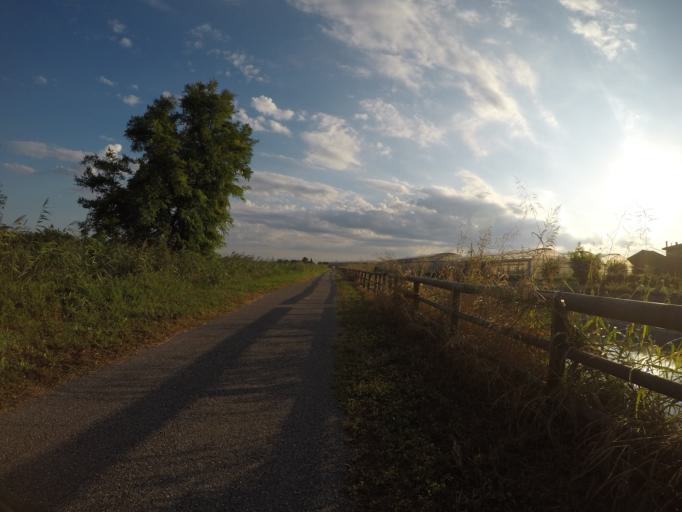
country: IT
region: Veneto
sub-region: Provincia di Rovigo
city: Lendinara
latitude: 45.0684
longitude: 11.6159
